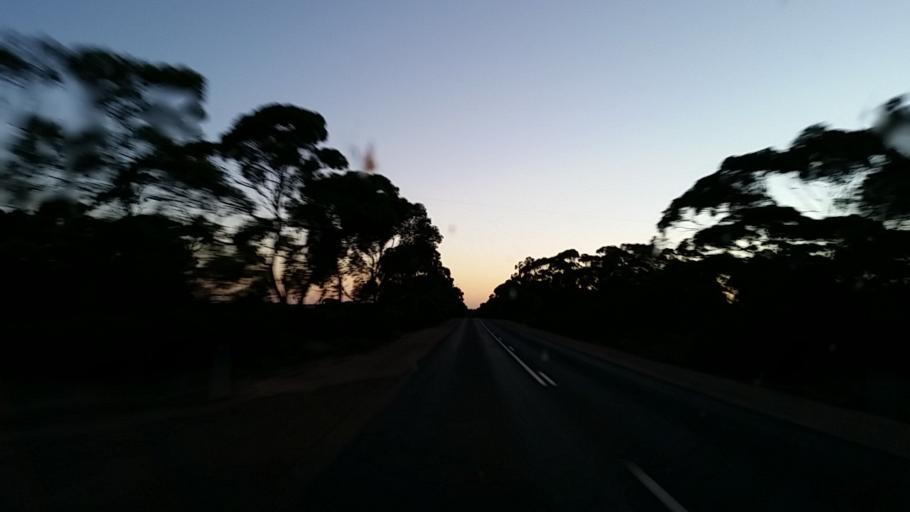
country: AU
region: South Australia
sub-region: Wakefield
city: Balaklava
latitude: -34.0984
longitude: 138.4961
